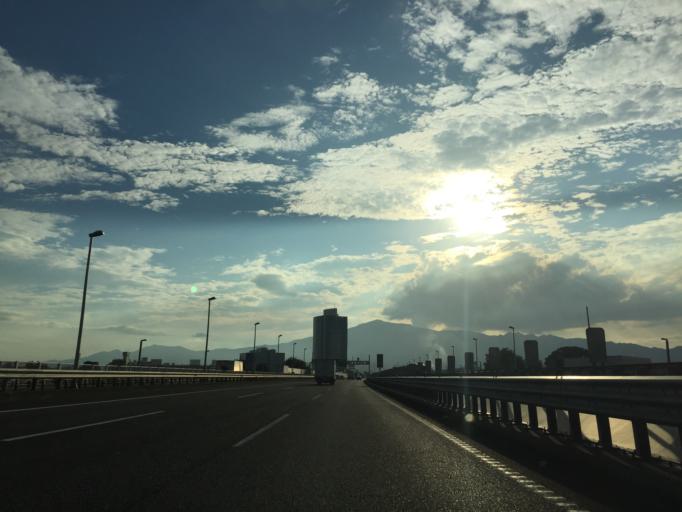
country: JP
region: Kanagawa
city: Atsugi
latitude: 35.4226
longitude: 139.3720
